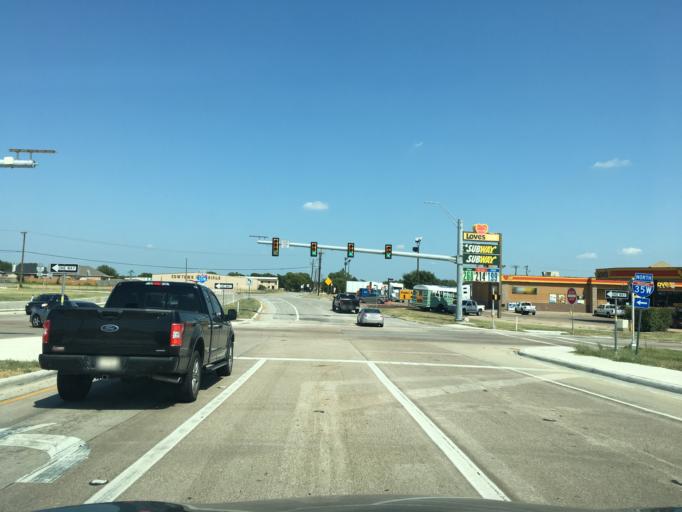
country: US
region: Texas
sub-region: Tarrant County
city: Everman
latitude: 32.5992
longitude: -97.3186
